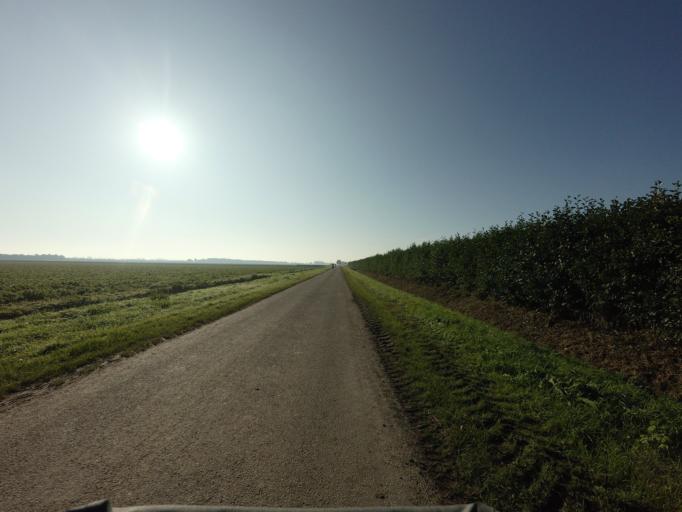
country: NL
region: North Brabant
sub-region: Gemeente Werkendam
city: Werkendam
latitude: 51.7928
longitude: 4.8820
